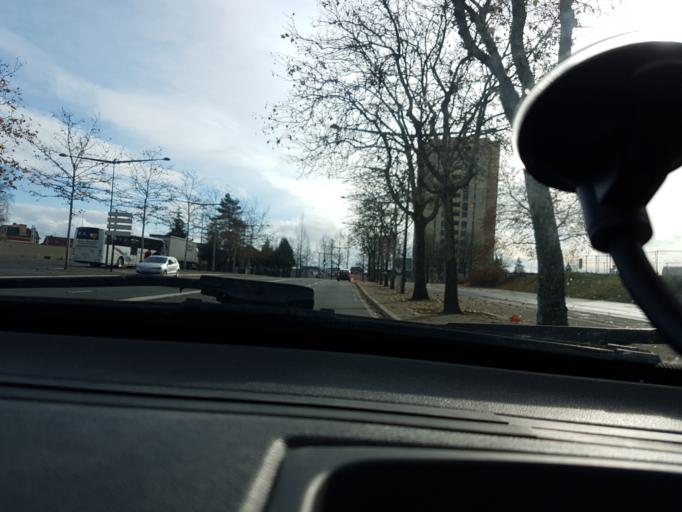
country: FR
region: Franche-Comte
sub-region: Territoire de Belfort
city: Bavilliers
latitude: 47.6294
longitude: 6.8430
